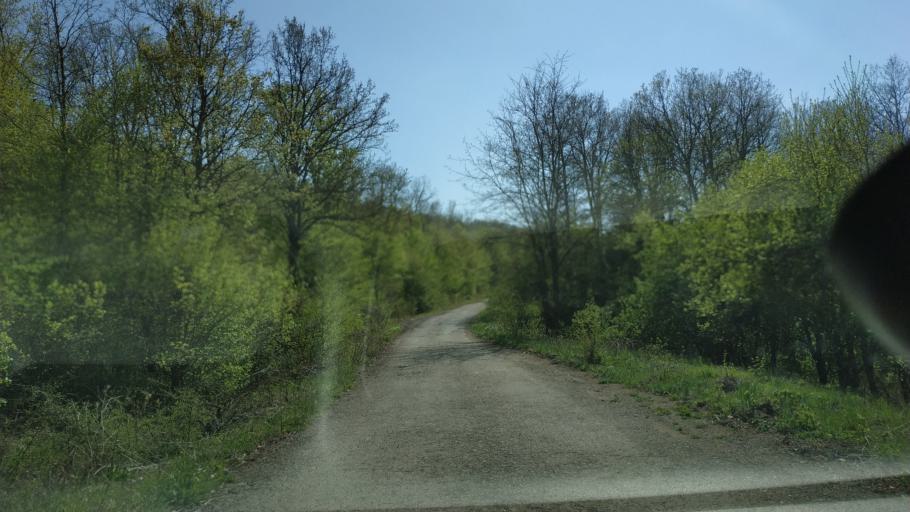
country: RS
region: Central Serbia
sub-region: Zajecarski Okrug
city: Soko Banja
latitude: 43.5084
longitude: 21.8999
